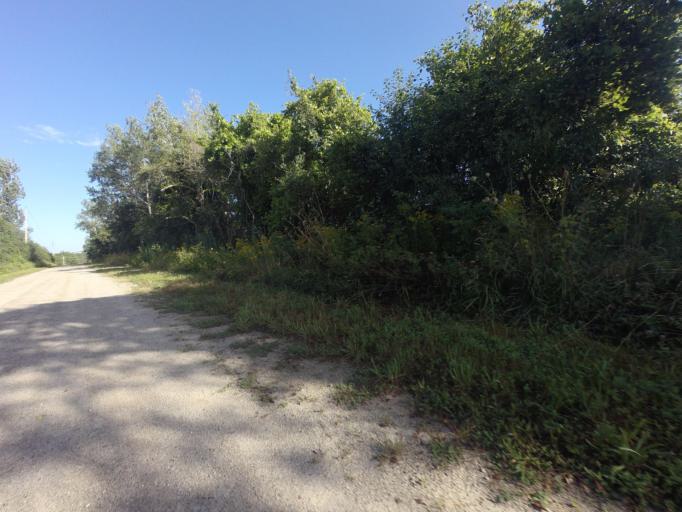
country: CA
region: Ontario
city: Waterloo
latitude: 43.6679
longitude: -80.4393
